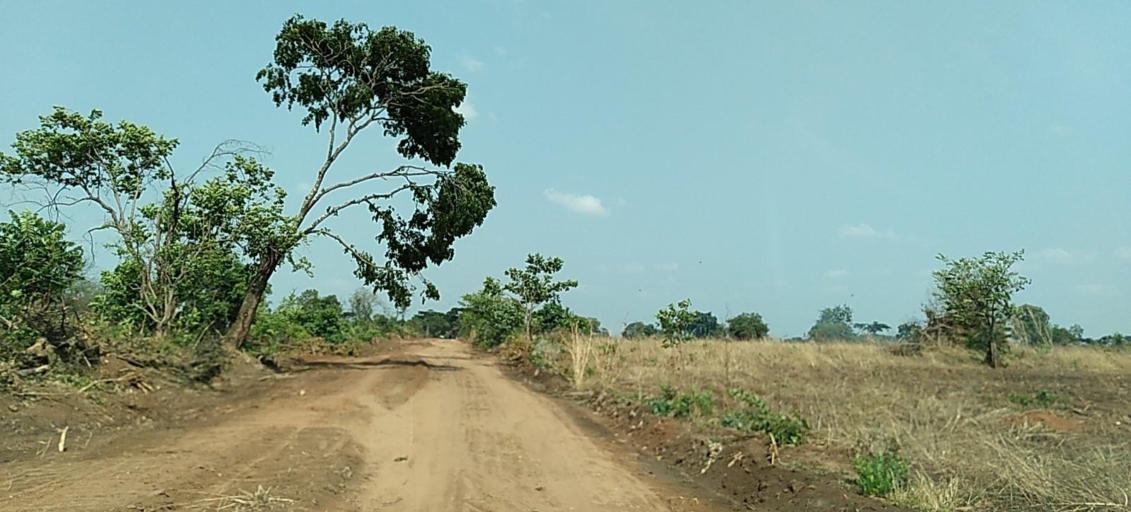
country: ZM
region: Copperbelt
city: Luanshya
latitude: -13.0895
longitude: 28.2647
